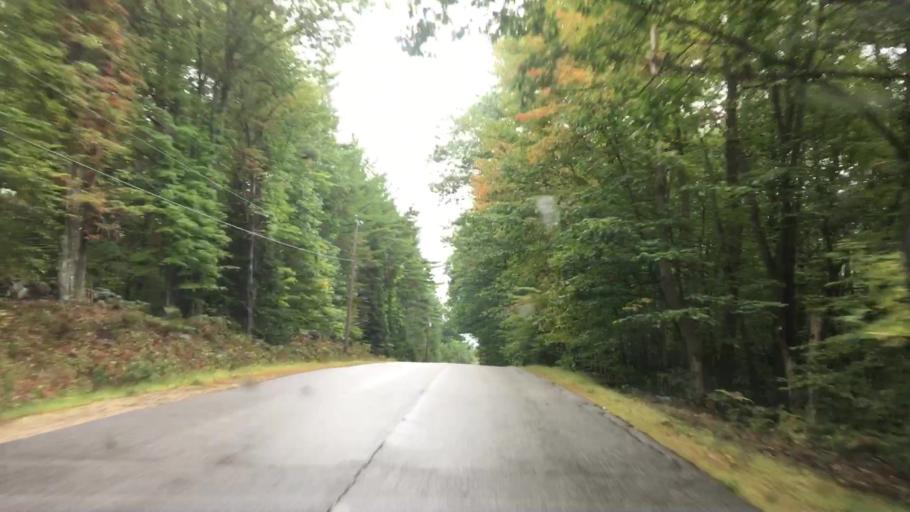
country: US
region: Maine
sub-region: Cumberland County
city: Harrison
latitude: 44.0584
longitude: -70.6224
